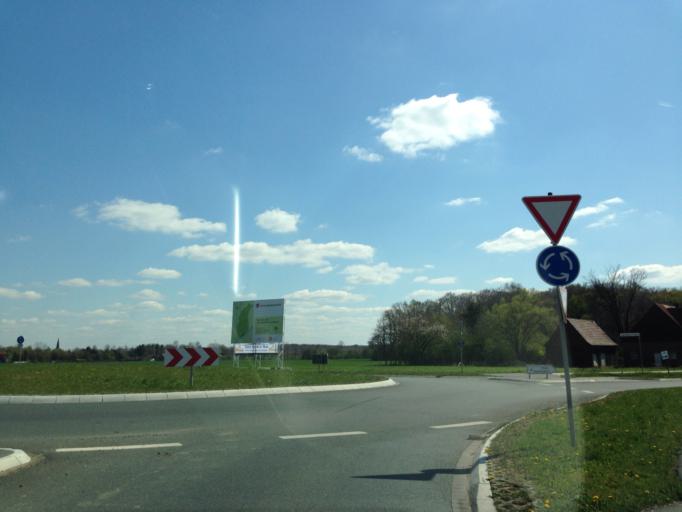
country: DE
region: North Rhine-Westphalia
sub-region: Regierungsbezirk Munster
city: Muenster
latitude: 51.8929
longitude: 7.5847
